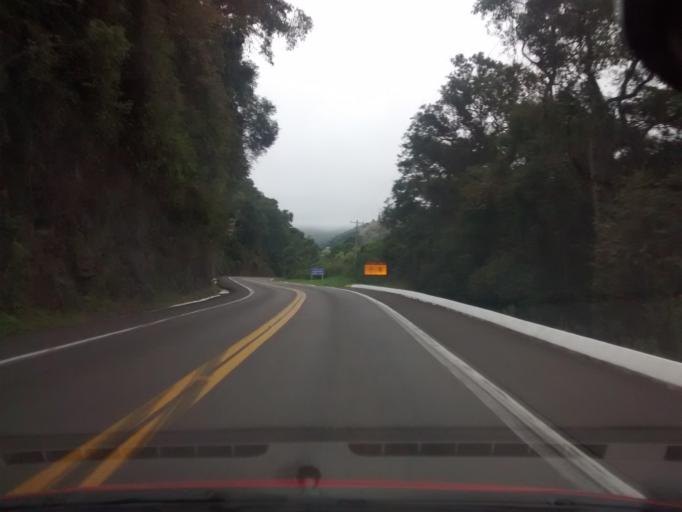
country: BR
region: Rio Grande do Sul
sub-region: Vacaria
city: Estrela
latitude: -28.2184
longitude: -50.7579
